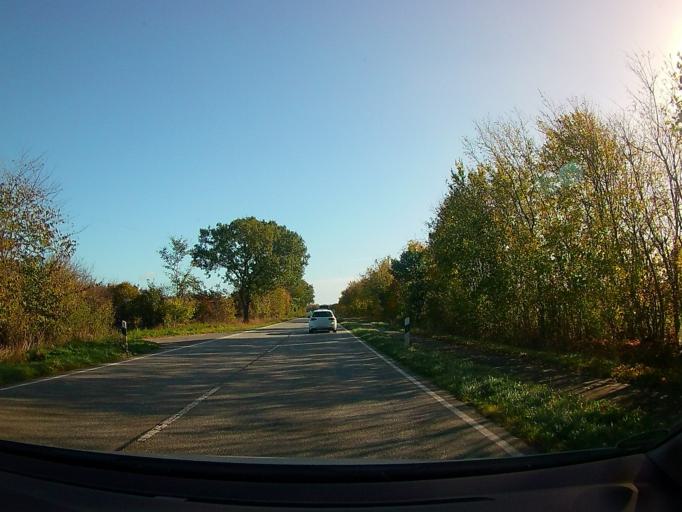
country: DE
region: Schleswig-Holstein
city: Schuby
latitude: 54.5189
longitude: 9.4595
